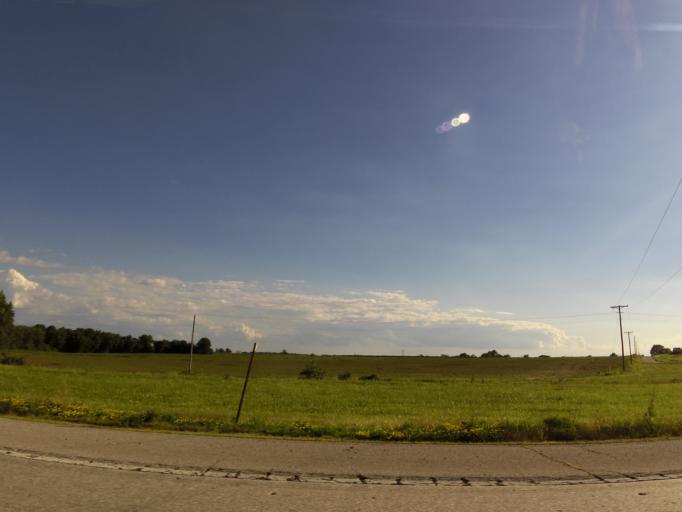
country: US
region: Missouri
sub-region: Pike County
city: Bowling Green
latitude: 39.2659
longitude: -91.0779
